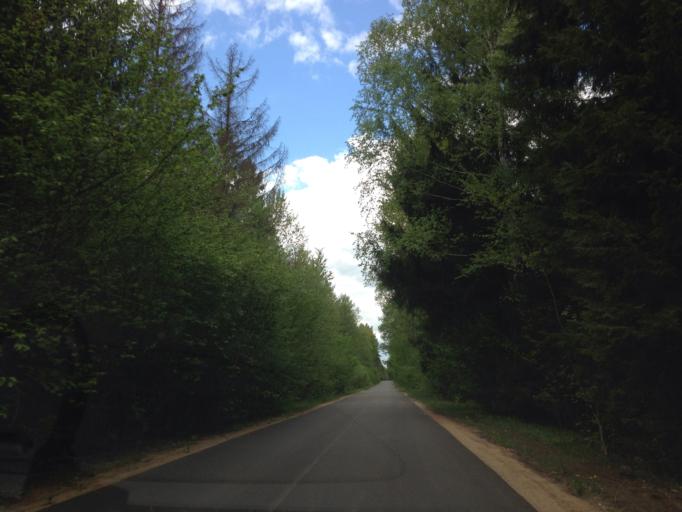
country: PL
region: Podlasie
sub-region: Powiat grajewski
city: Radzilow
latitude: 53.3306
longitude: 22.5999
